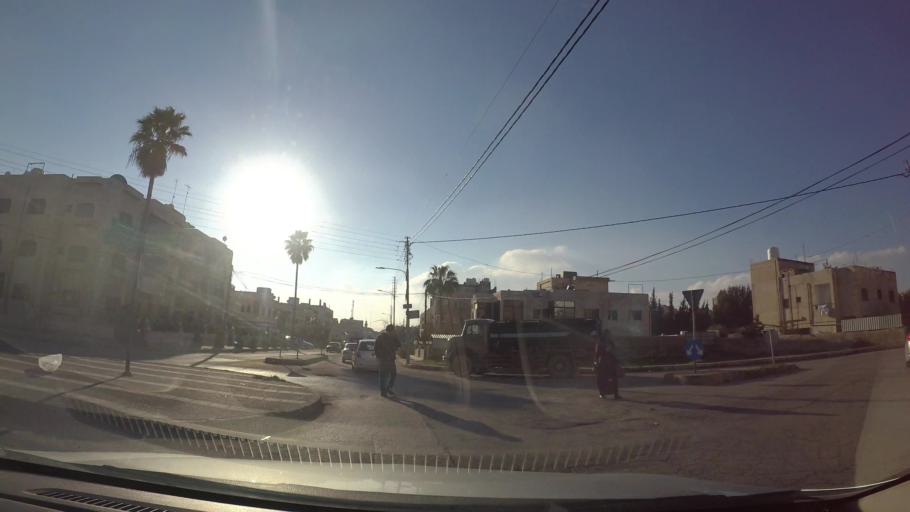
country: JO
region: Amman
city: Al Bunayyat ash Shamaliyah
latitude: 31.9029
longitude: 35.9113
